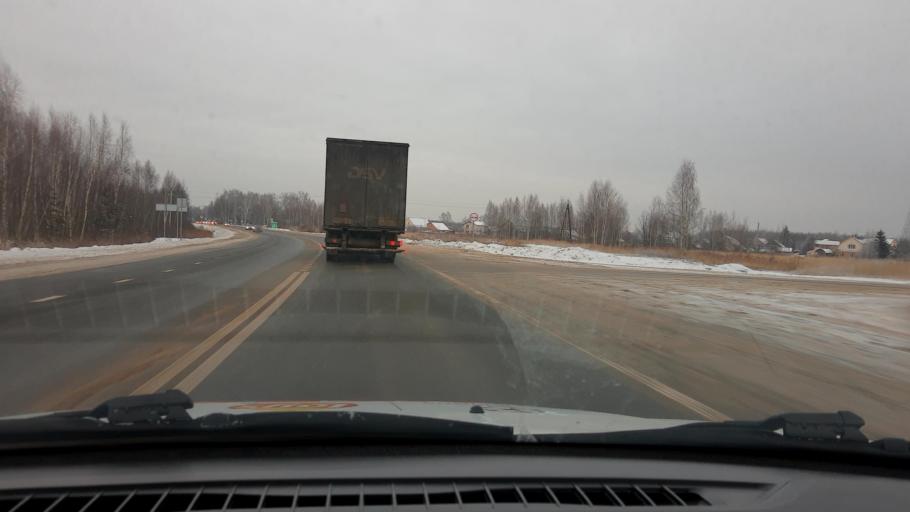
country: RU
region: Nizjnij Novgorod
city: Sitniki
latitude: 56.5244
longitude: 44.0264
